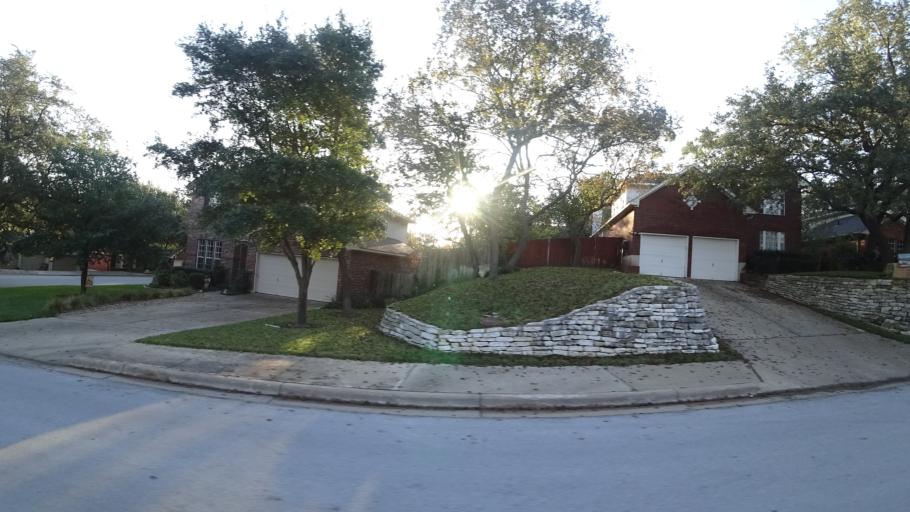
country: US
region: Texas
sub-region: Travis County
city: Hudson Bend
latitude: 30.3812
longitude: -97.8919
